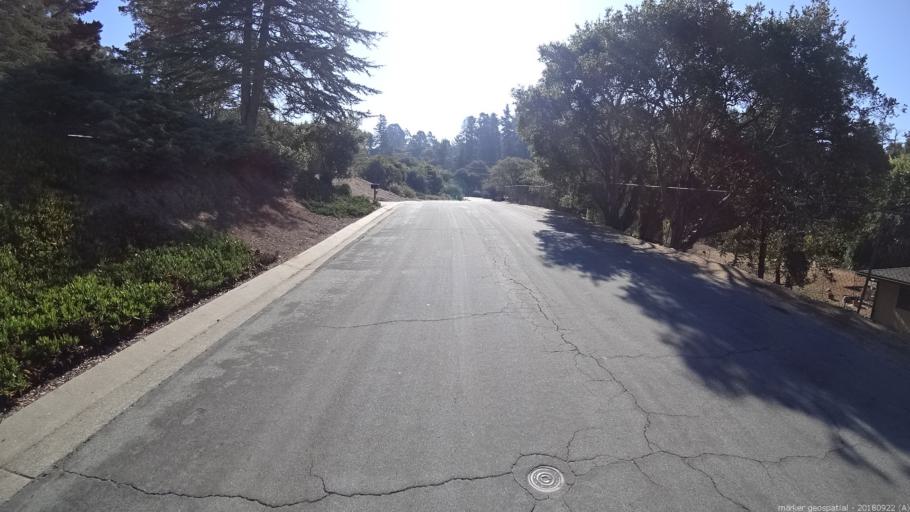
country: US
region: California
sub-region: Monterey County
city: Prunedale
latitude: 36.8226
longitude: -121.6426
